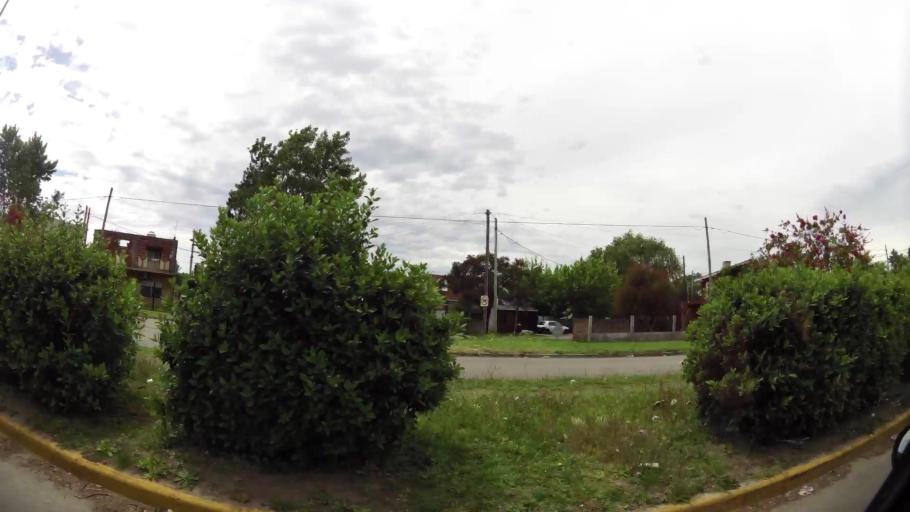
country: AR
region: Buenos Aires
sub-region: Partido de Quilmes
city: Quilmes
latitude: -34.7630
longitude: -58.2354
